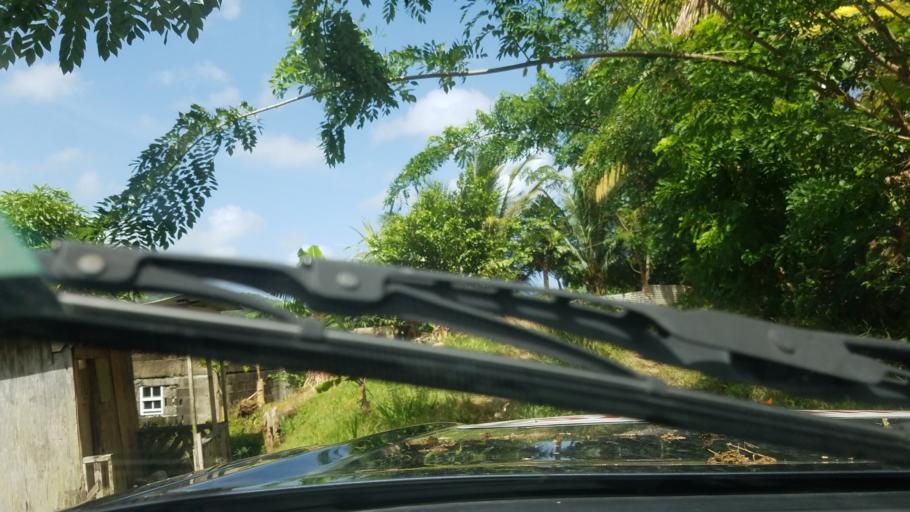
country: LC
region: Anse-la-Raye
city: Anse La Raye
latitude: 13.9477
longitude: -60.9887
